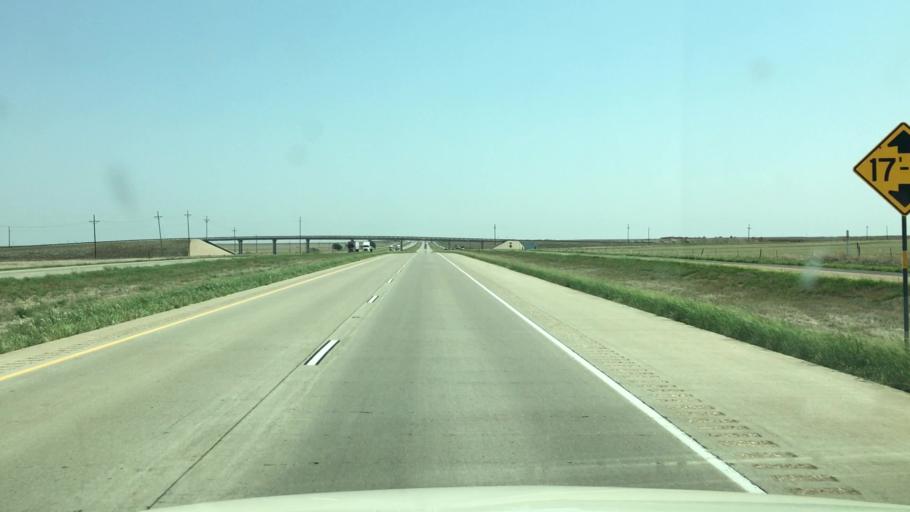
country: US
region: Texas
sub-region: Oldham County
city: Vega
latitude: 35.2332
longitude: -102.3692
